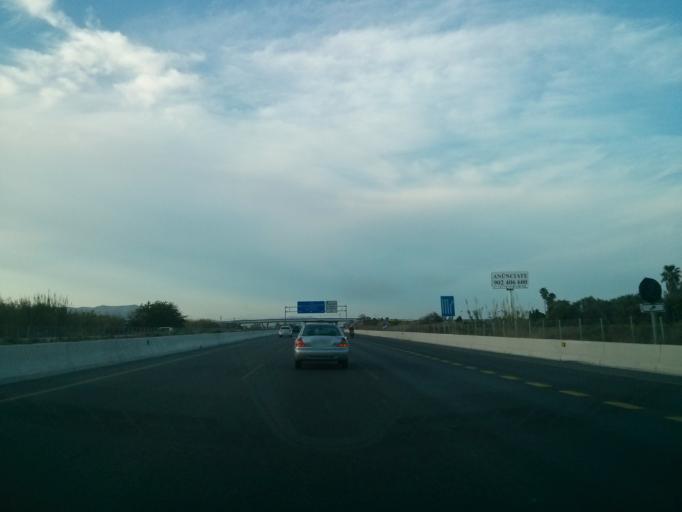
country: ES
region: Valencia
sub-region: Provincia de Valencia
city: Puig
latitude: 39.5649
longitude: -0.2961
